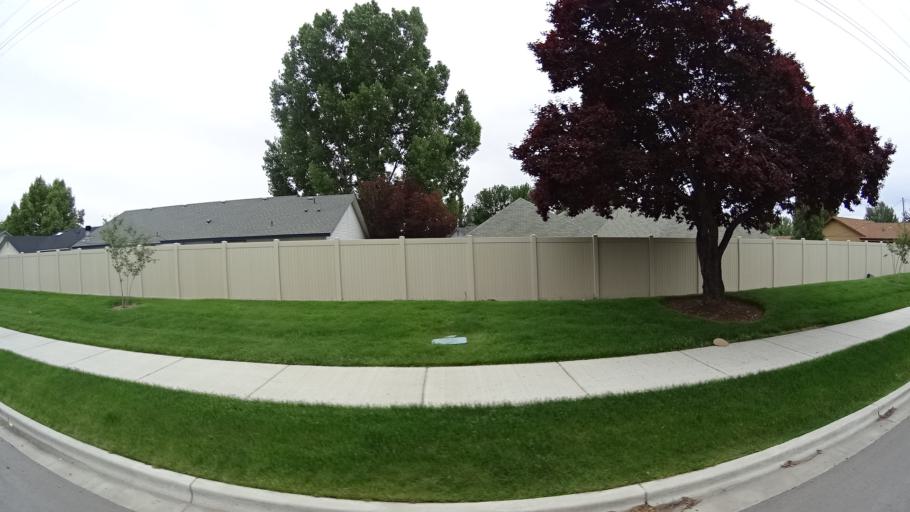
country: US
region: Idaho
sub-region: Ada County
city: Meridian
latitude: 43.6337
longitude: -116.3893
